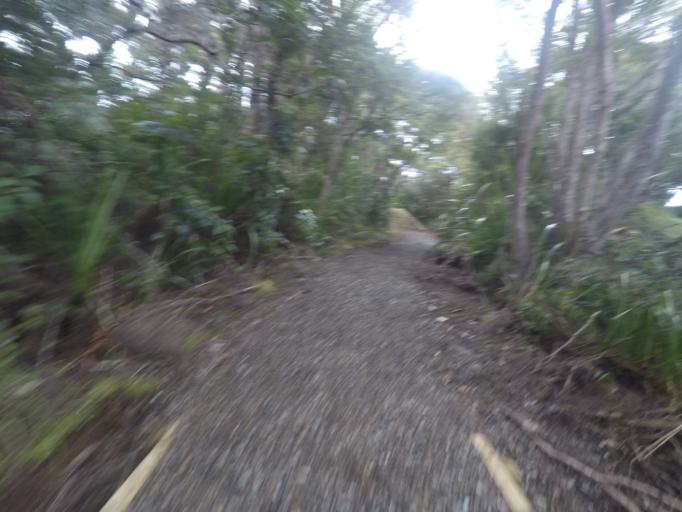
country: NZ
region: Auckland
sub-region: Auckland
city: Titirangi
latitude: -37.0002
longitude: 174.5416
